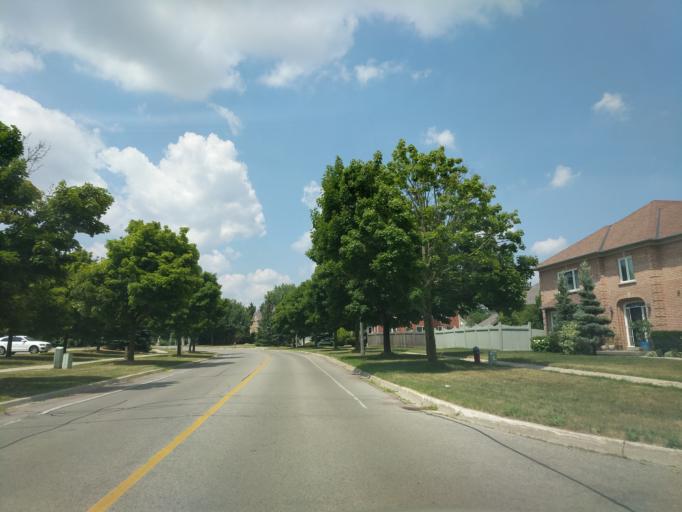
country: CA
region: Ontario
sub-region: York
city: Richmond Hill
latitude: 43.8697
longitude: -79.4010
